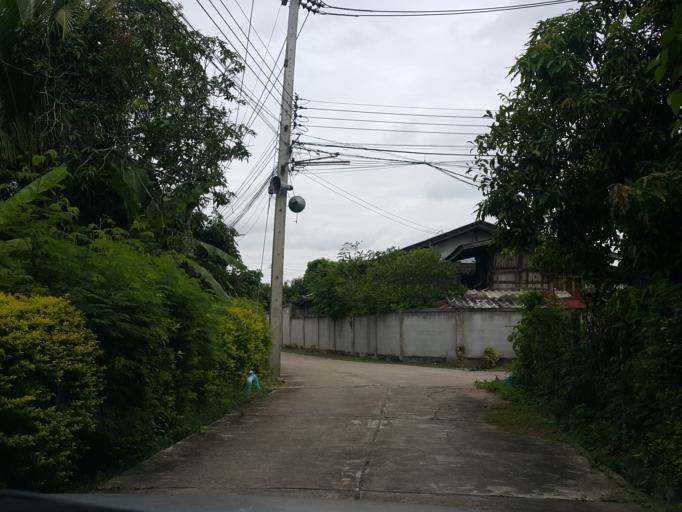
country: TH
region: Chiang Mai
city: San Sai
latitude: 18.8399
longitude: 99.1227
